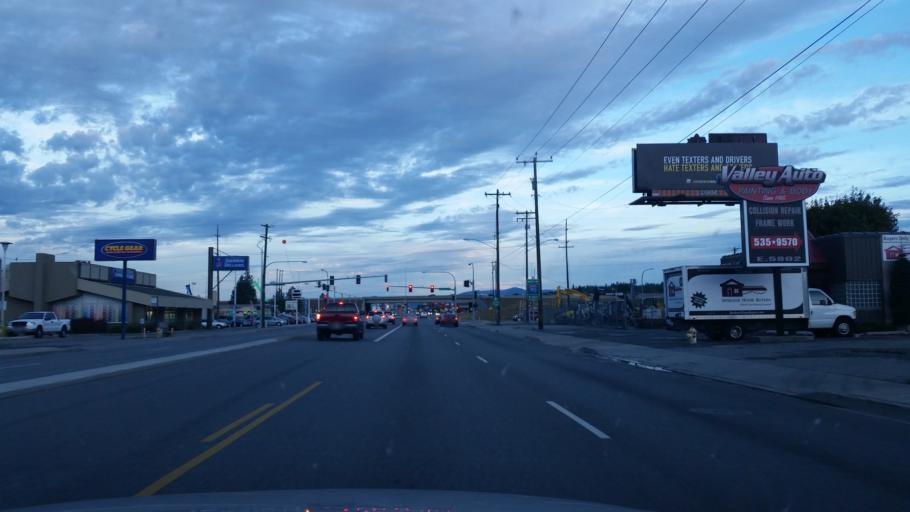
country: US
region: Washington
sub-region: Spokane County
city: Millwood
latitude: 47.6570
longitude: -117.3273
